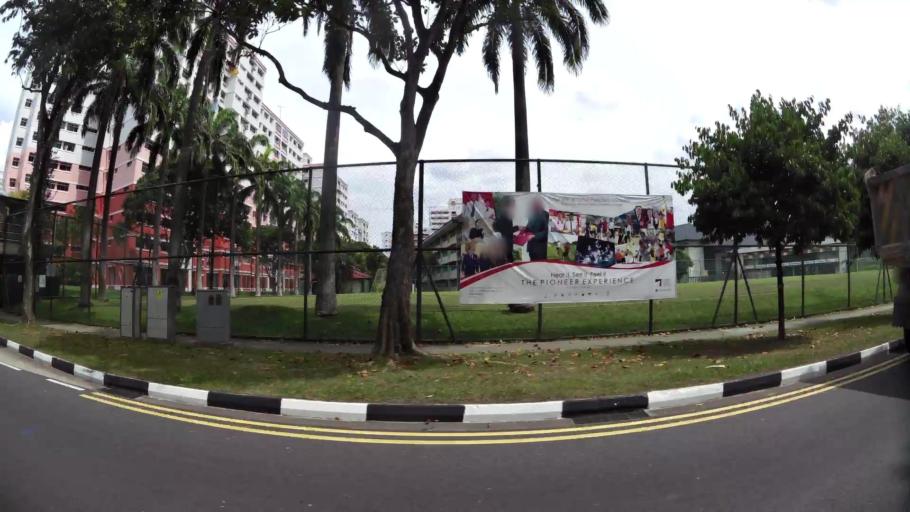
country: MY
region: Johor
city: Johor Bahru
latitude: 1.3913
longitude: 103.7403
